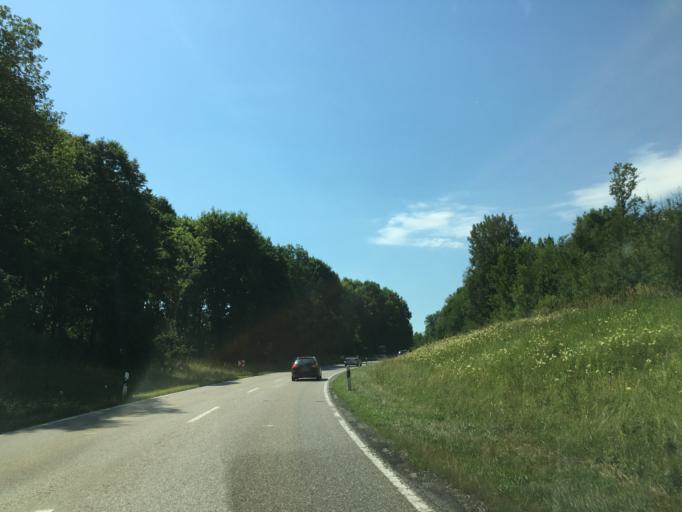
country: DE
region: Bavaria
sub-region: Upper Bavaria
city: Griesstatt
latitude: 47.9931
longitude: 12.1661
